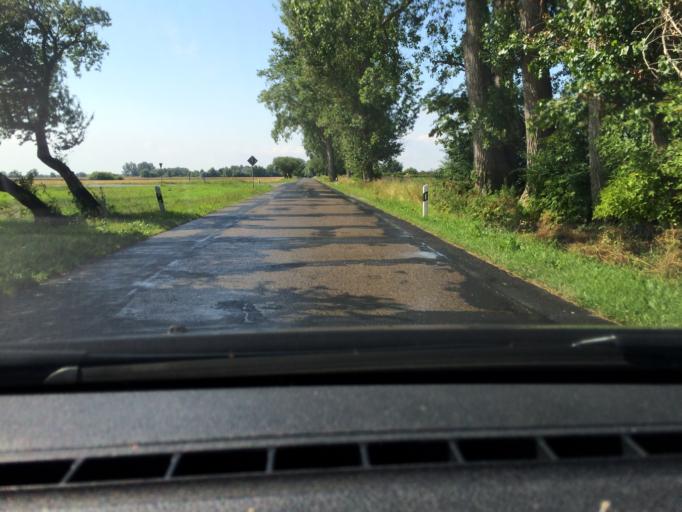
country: DE
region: Mecklenburg-Vorpommern
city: Niepars
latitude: 54.3538
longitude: 12.9023
